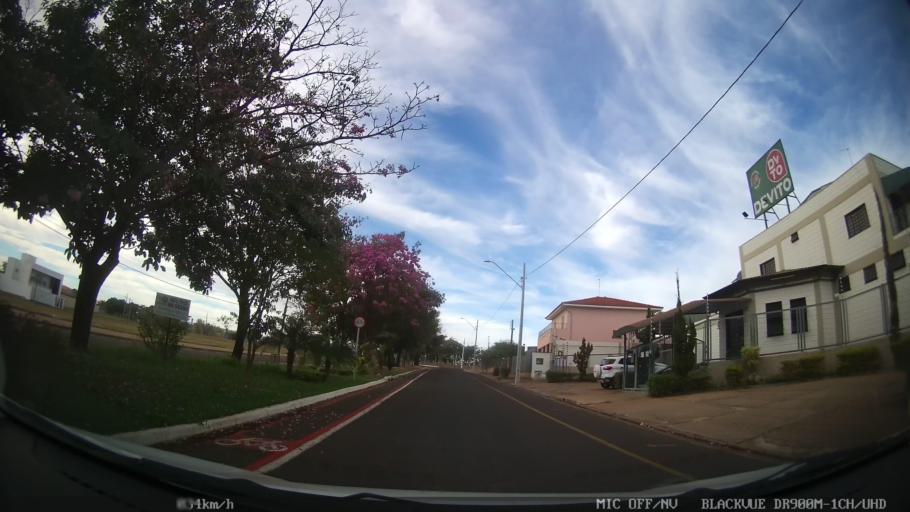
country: BR
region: Sao Paulo
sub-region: Catanduva
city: Catanduva
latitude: -21.1513
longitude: -48.9937
